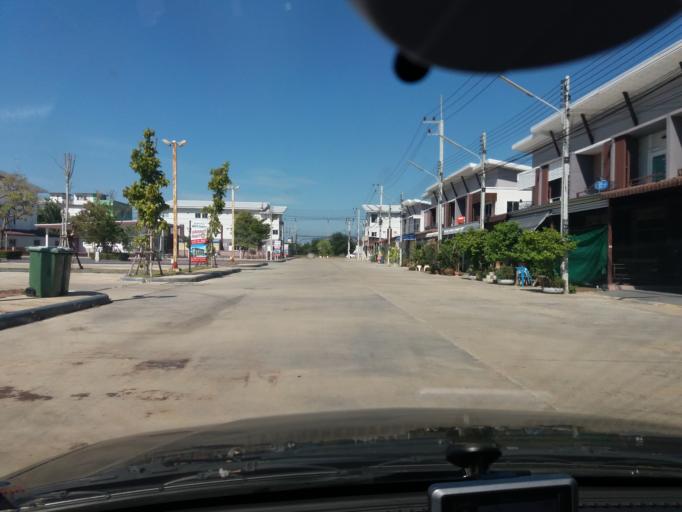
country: TH
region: Suphan Buri
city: Suphan Buri
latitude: 14.4609
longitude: 100.1462
